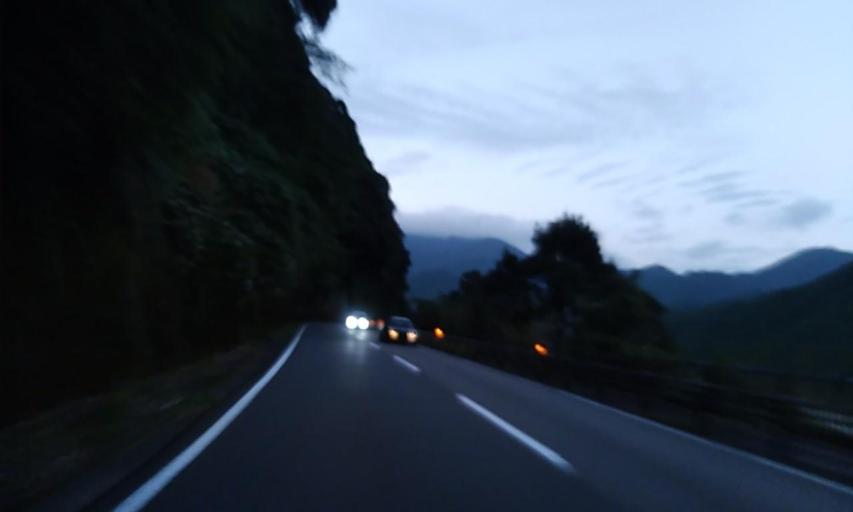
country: JP
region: Wakayama
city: Shingu
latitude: 33.7402
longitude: 135.9388
